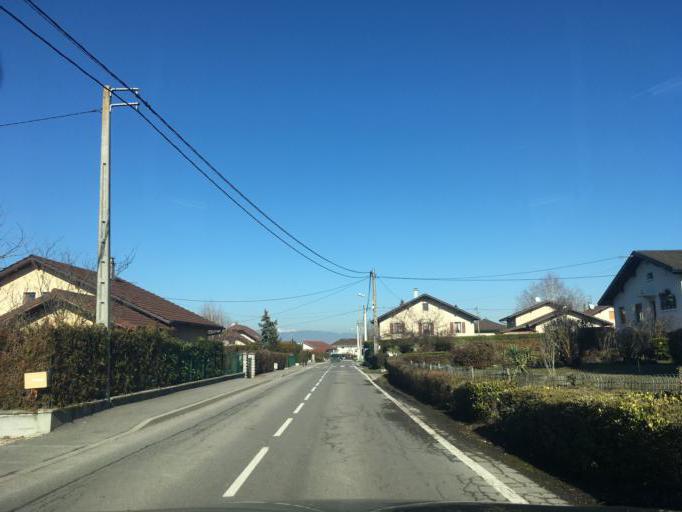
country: FR
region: Rhone-Alpes
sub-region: Departement de la Haute-Savoie
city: Cranves-Sales
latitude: 46.1884
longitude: 6.2916
